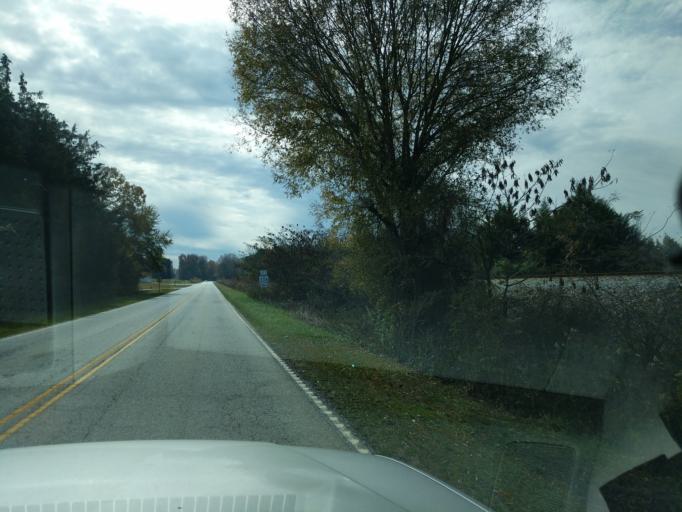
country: US
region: South Carolina
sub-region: Laurens County
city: Watts Mills
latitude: 34.5858
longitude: -81.9950
